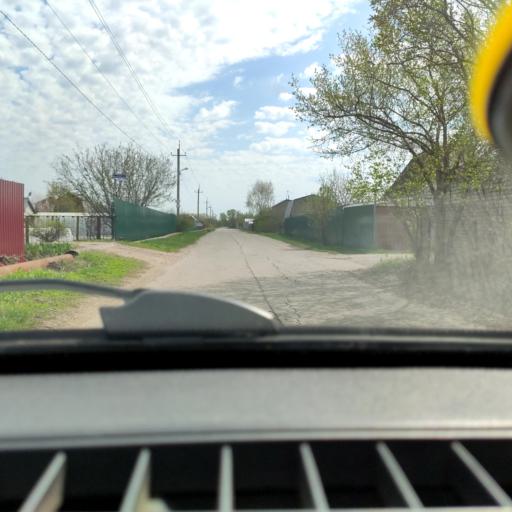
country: RU
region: Samara
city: Tol'yatti
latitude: 53.6993
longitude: 49.4450
